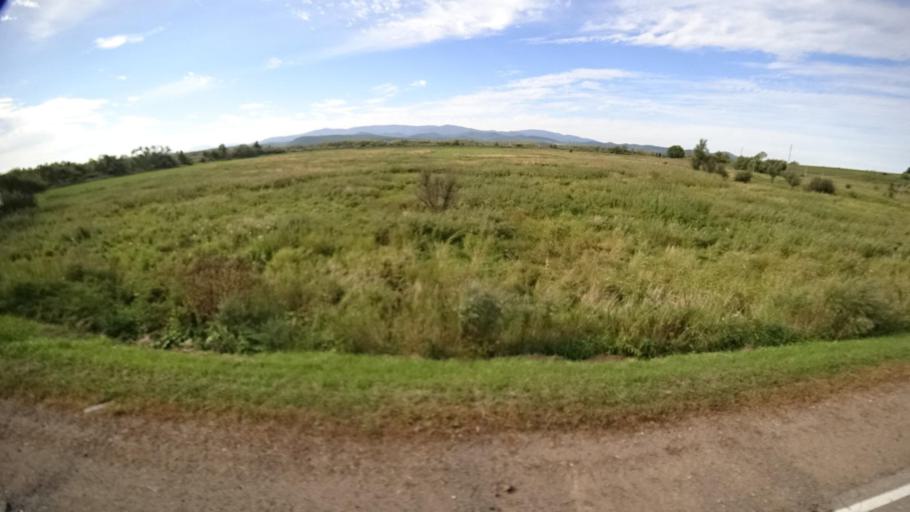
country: RU
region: Primorskiy
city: Dostoyevka
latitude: 44.3120
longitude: 133.4579
